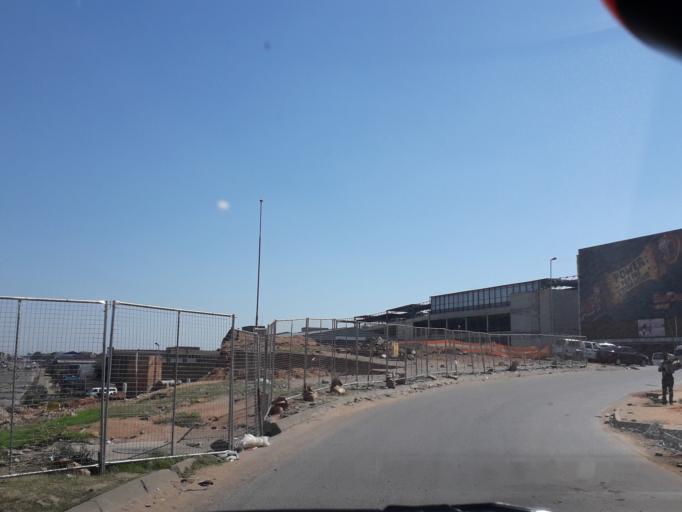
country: ZA
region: Gauteng
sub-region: City of Johannesburg Metropolitan Municipality
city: Modderfontein
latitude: -26.1105
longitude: 28.0850
